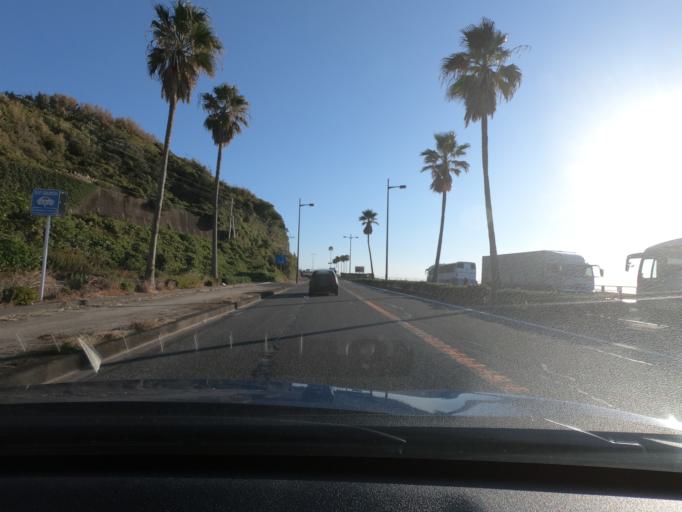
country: JP
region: Kagoshima
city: Akune
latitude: 31.9454
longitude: 130.2166
